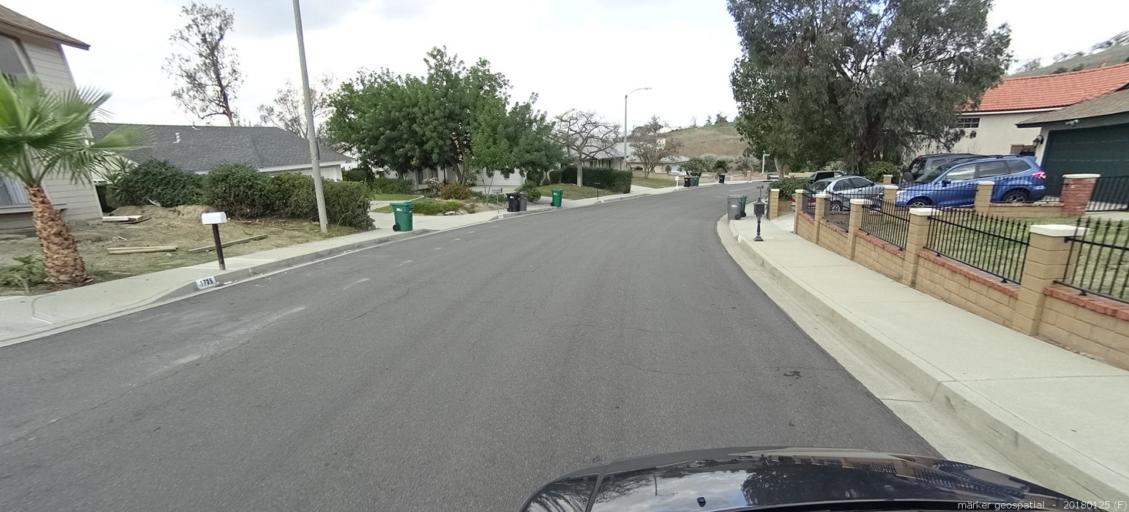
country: US
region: California
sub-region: Los Angeles County
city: Walnut
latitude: 33.9898
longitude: -117.8415
